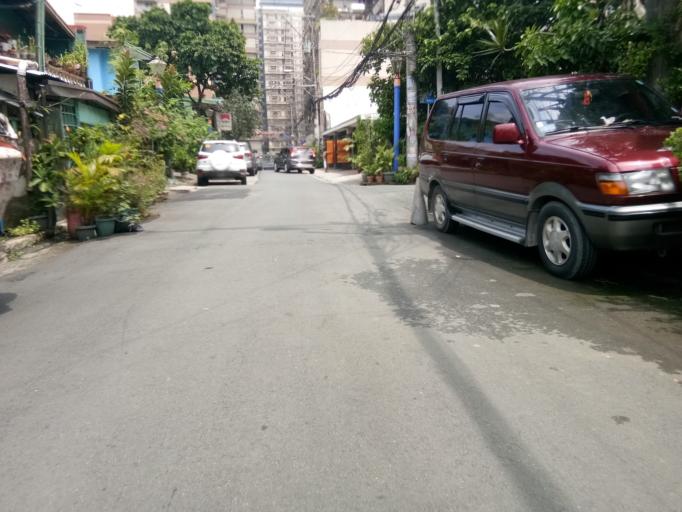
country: PH
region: Metro Manila
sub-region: San Juan
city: San Juan
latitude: 14.6082
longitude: 121.0471
